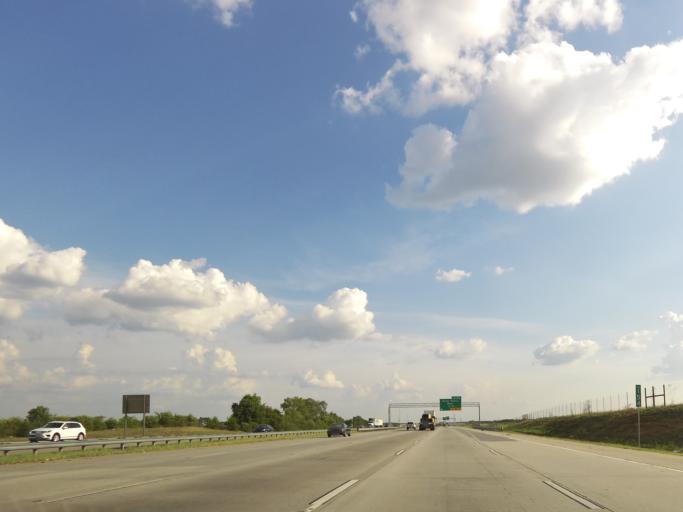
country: US
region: Georgia
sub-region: Peach County
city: Byron
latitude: 32.7250
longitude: -83.7270
